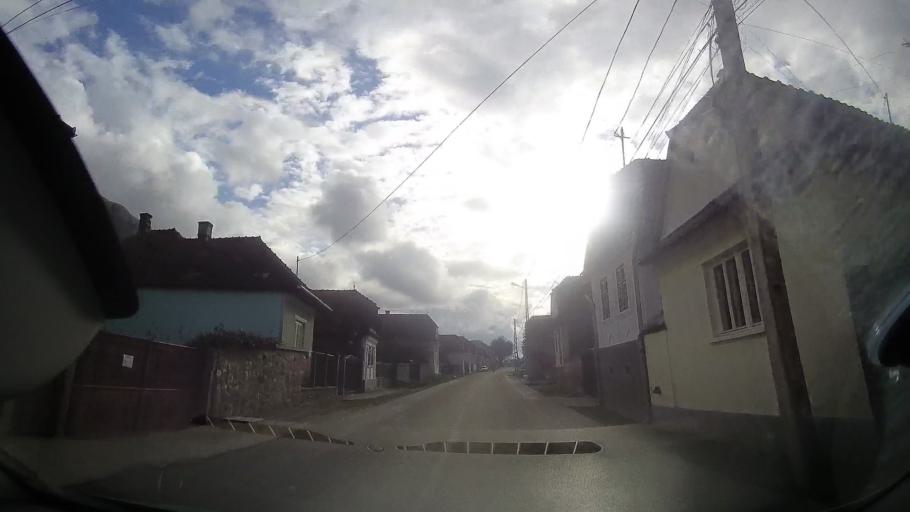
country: RO
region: Alba
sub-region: Comuna Rimetea
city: Rimetea
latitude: 46.4548
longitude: 23.5682
